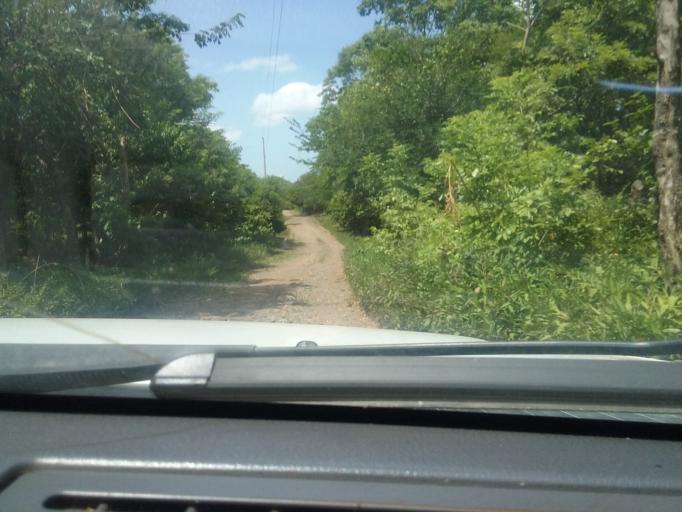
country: NI
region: Matagalpa
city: Terrabona
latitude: 12.6559
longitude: -85.9914
